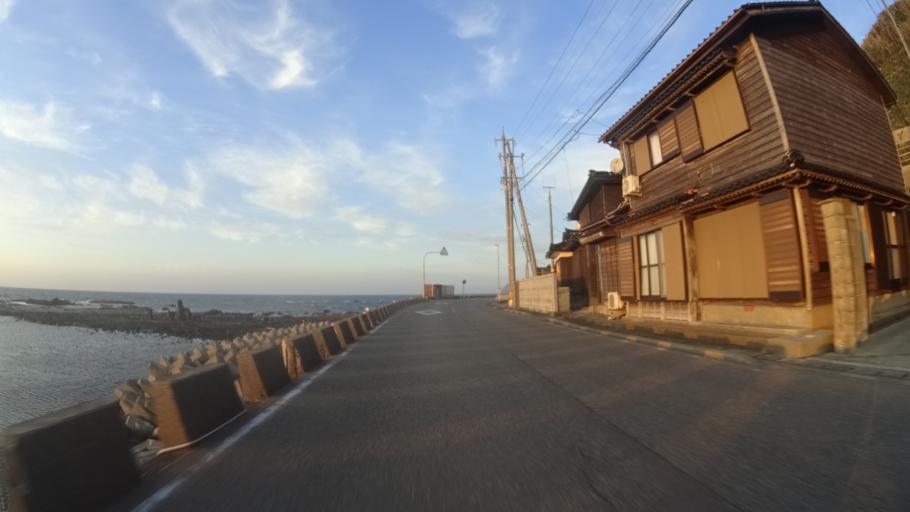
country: JP
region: Ishikawa
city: Nanao
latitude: 37.2409
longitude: 136.7015
